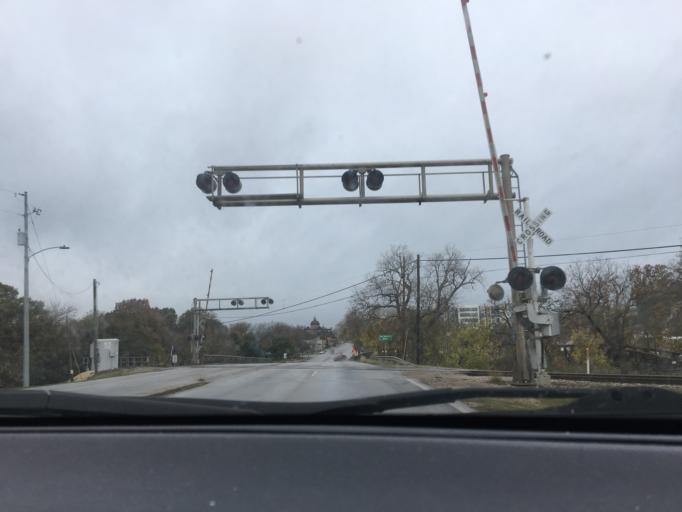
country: US
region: Texas
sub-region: Hays County
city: San Marcos
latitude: 29.8842
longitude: -97.9346
